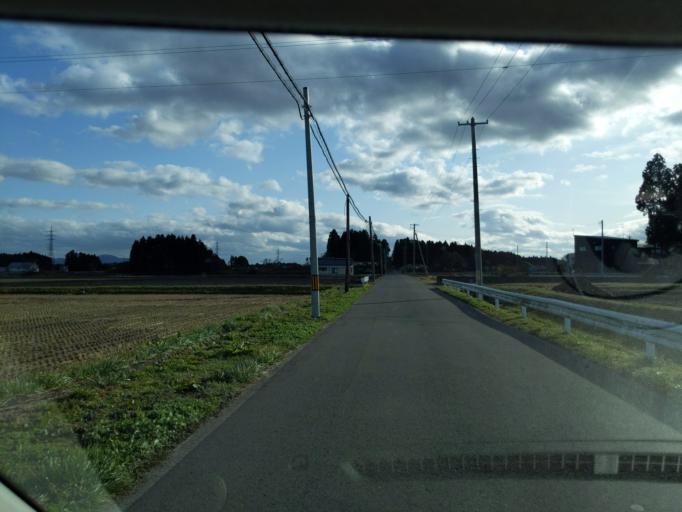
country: JP
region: Iwate
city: Mizusawa
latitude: 39.1312
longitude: 141.0807
